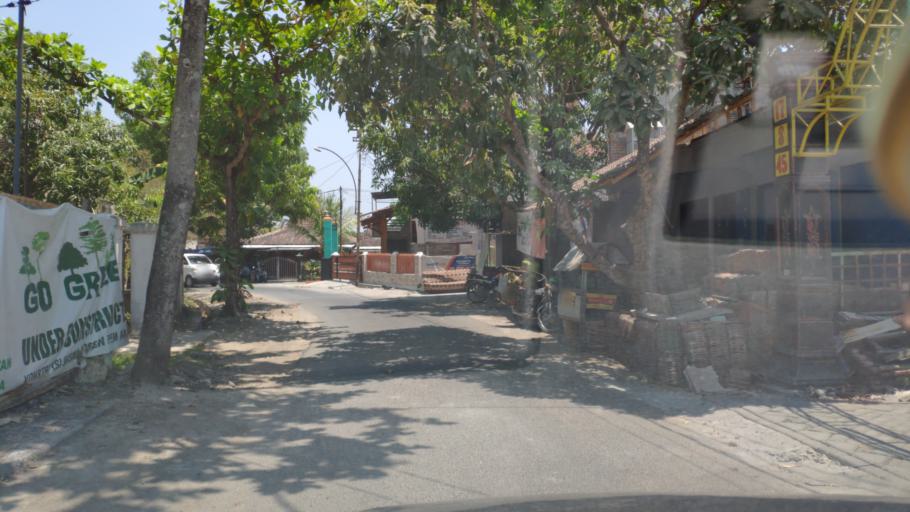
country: ID
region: Central Java
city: Cepu
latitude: -7.1477
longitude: 111.5877
